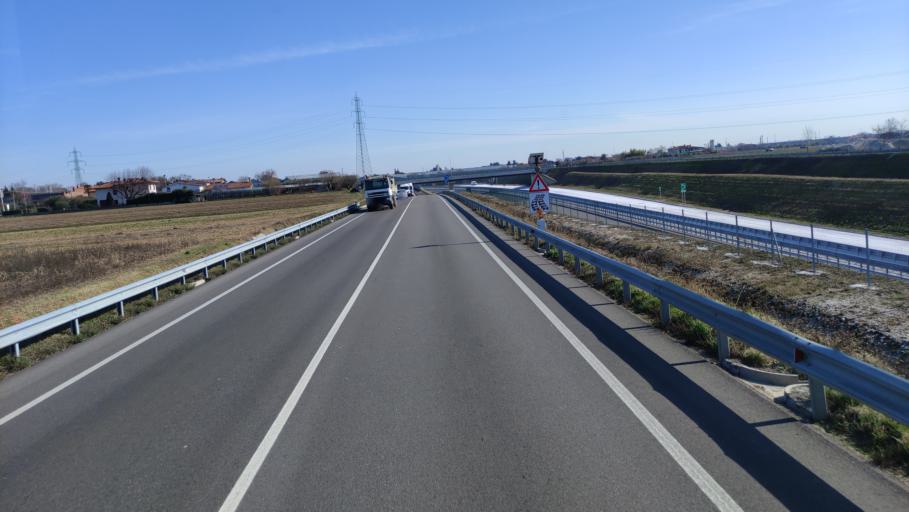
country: IT
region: Veneto
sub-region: Provincia di Vicenza
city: San Zeno-San Giuseppe
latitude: 45.7364
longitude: 11.7464
